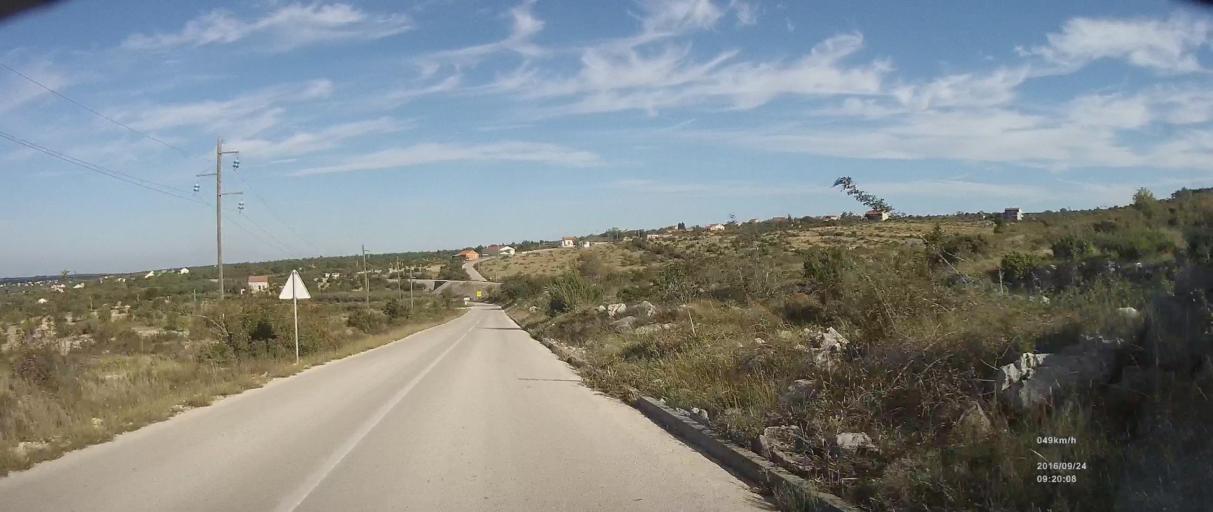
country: HR
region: Zadarska
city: Polaca
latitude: 44.0664
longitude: 15.4987
